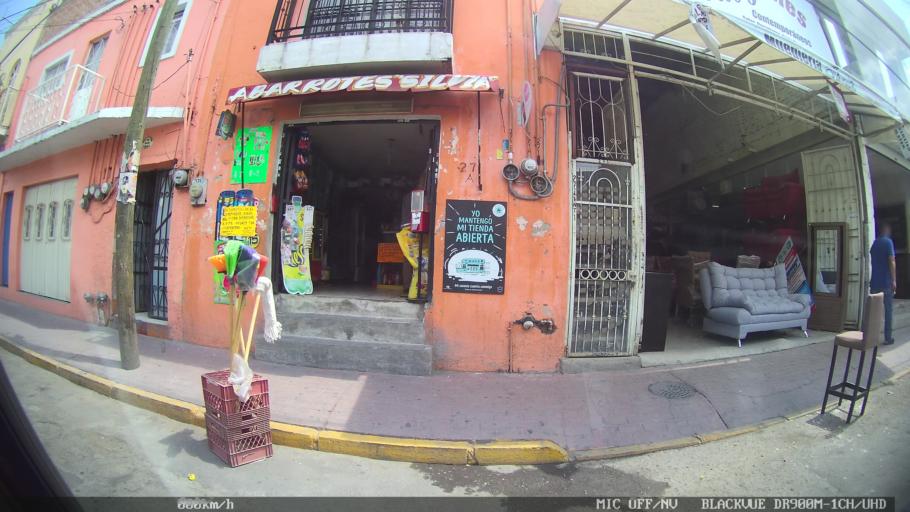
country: MX
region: Jalisco
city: Tonala
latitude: 20.6252
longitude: -103.2476
